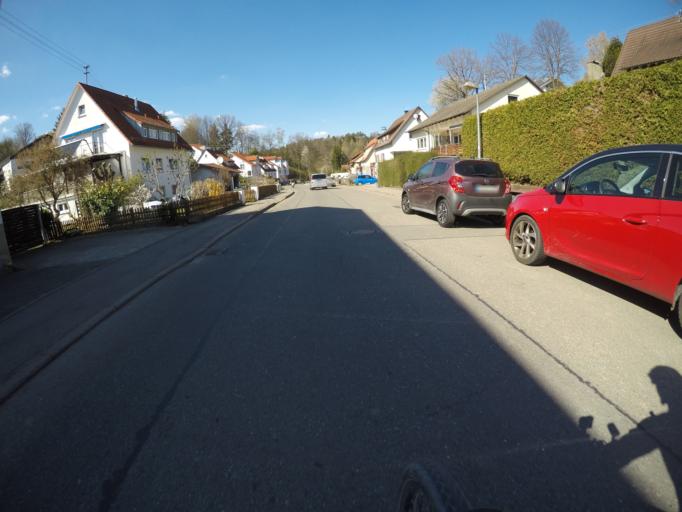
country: DE
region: Baden-Wuerttemberg
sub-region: Regierungsbezirk Stuttgart
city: Waldenbuch
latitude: 48.6319
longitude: 9.1533
